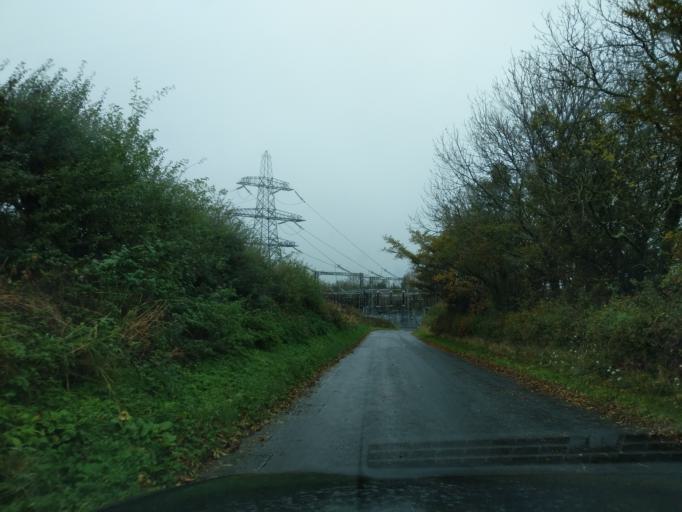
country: GB
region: Scotland
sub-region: East Lothian
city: Dunbar
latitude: 55.9498
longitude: -2.4189
